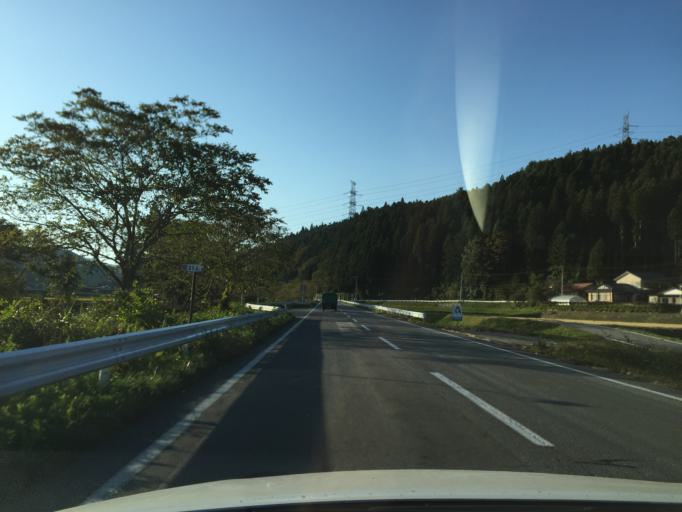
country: JP
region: Fukushima
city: Iwaki
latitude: 37.1350
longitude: 140.7091
